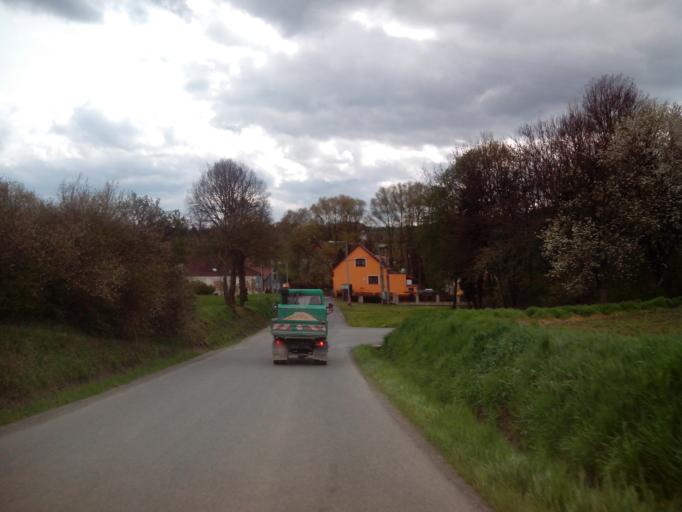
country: CZ
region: Central Bohemia
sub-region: Okres Beroun
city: Lodenice
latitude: 49.9127
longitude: 14.1532
